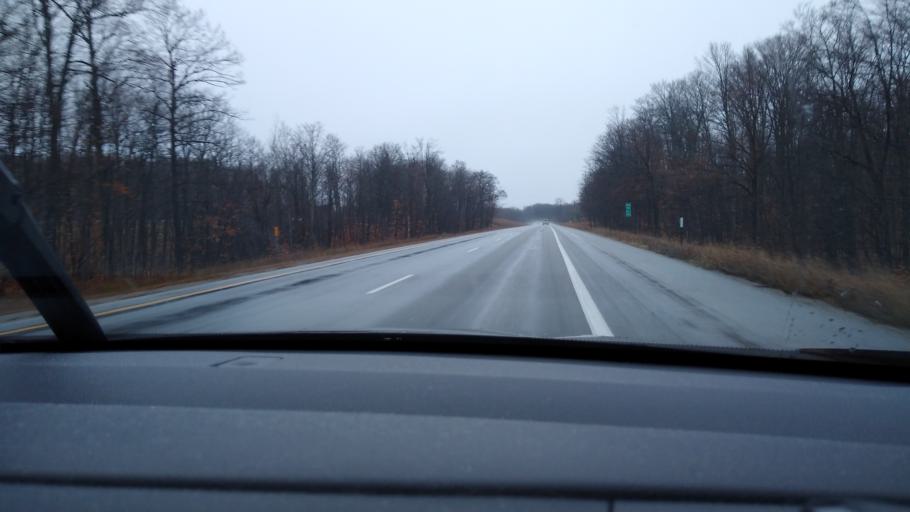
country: US
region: Michigan
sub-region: Cheboygan County
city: Indian River
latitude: 45.3339
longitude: -84.6063
